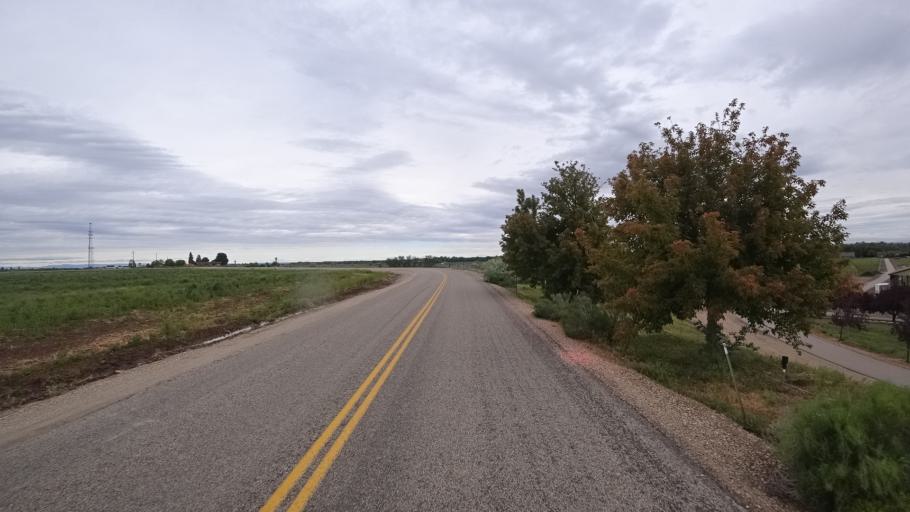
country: US
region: Idaho
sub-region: Ada County
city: Star
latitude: 43.6707
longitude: -116.5096
